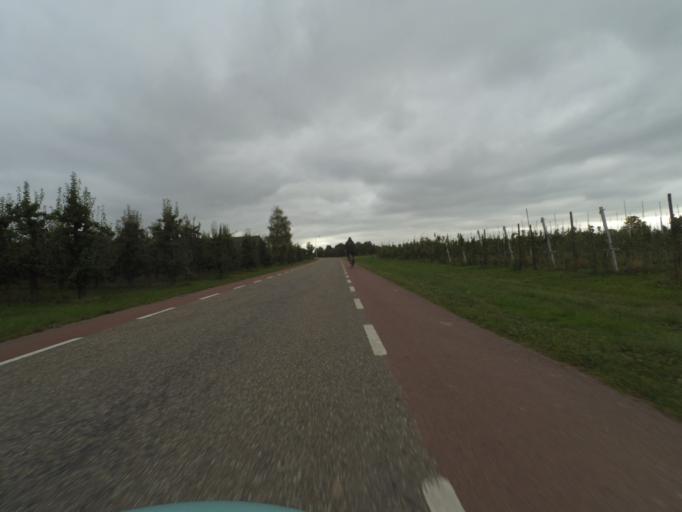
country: NL
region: Utrecht
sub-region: Gemeente Rhenen
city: Rhenen
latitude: 51.9443
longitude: 5.5493
